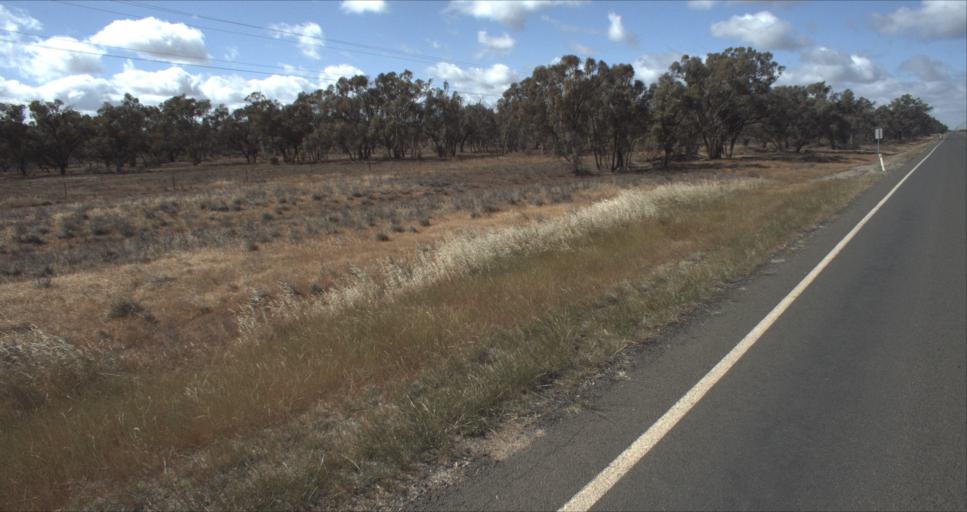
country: AU
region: New South Wales
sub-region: Murrumbidgee Shire
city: Darlington Point
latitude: -34.5204
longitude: 146.1758
